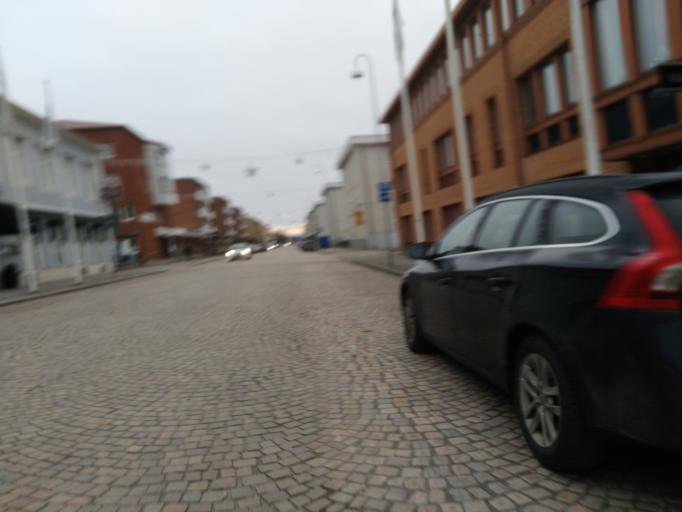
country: SE
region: Vaestra Goetaland
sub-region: Lidkopings Kommun
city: Lidkoping
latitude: 58.5022
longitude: 13.1636
